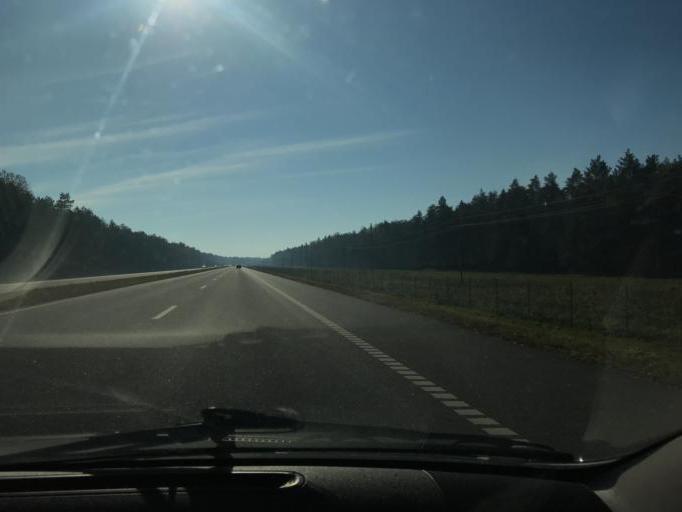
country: BY
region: Minsk
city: Slutsk
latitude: 53.2990
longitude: 27.5442
